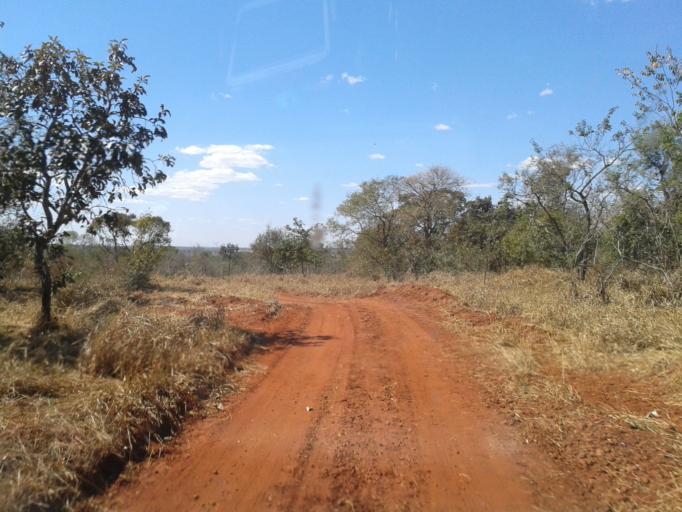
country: BR
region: Minas Gerais
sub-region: Santa Vitoria
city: Santa Vitoria
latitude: -19.0172
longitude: -50.4478
